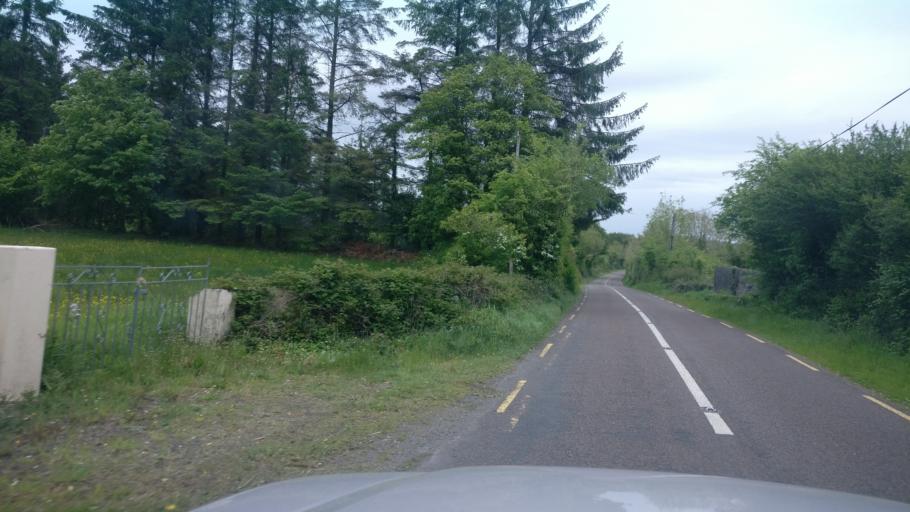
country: IE
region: Connaught
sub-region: County Galway
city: Loughrea
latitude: 53.0837
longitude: -8.5169
